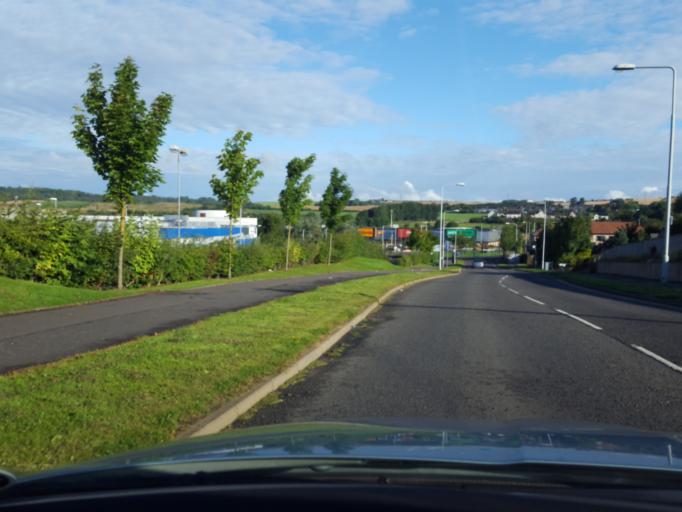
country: GB
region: Scotland
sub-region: Fife
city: Crossgates
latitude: 56.0787
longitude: -3.4054
